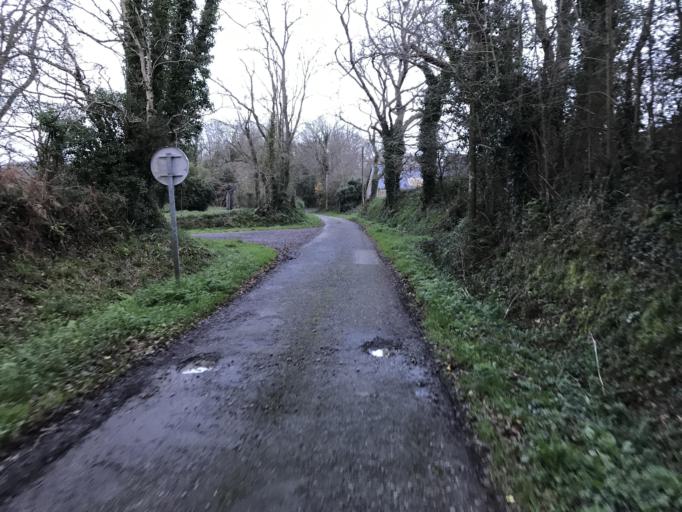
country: FR
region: Brittany
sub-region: Departement du Finistere
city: Loperhet
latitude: 48.3654
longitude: -4.3165
